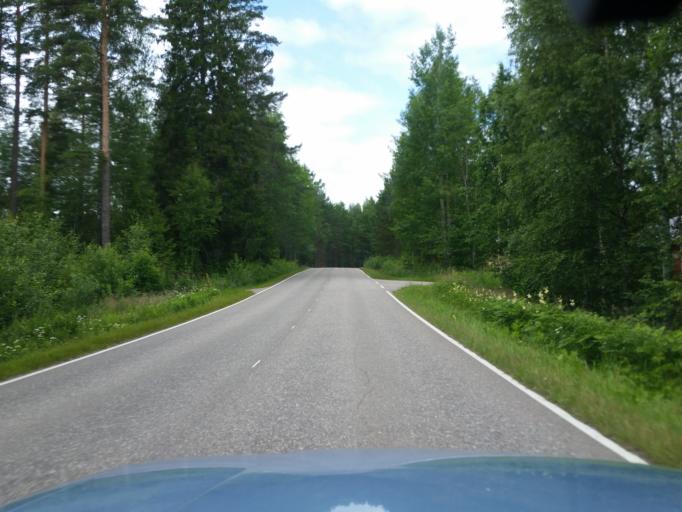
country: FI
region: Southern Savonia
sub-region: Savonlinna
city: Sulkava
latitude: 61.7926
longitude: 28.3878
